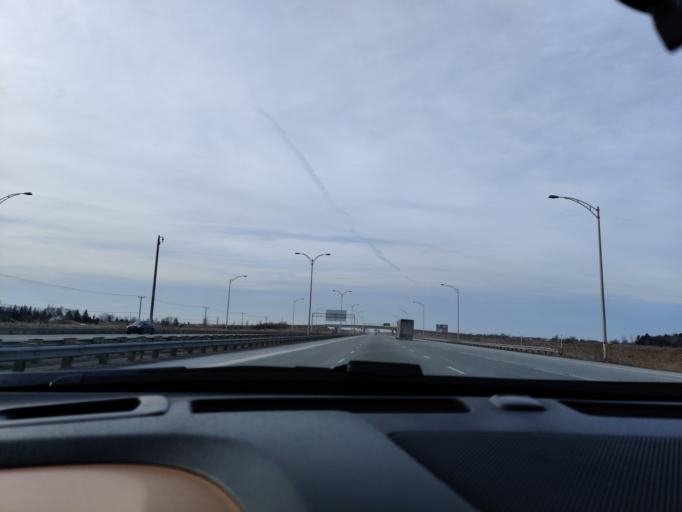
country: CA
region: Quebec
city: Les Cedres
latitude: 45.3511
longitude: -74.0624
